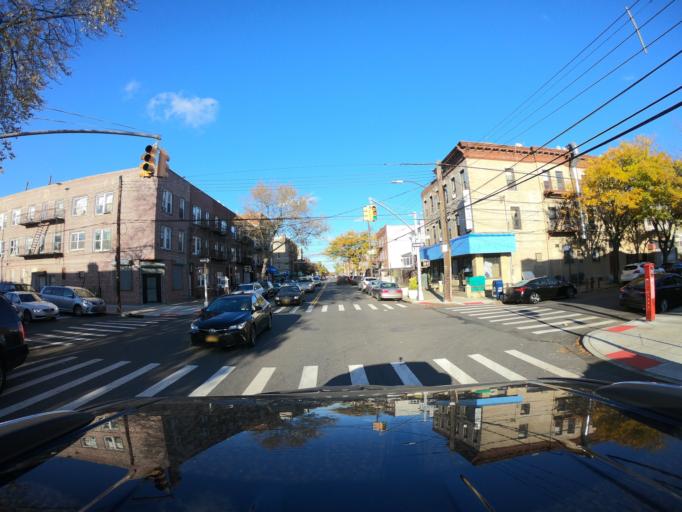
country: US
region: New York
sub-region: Kings County
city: Bensonhurst
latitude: 40.6223
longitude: -74.0018
